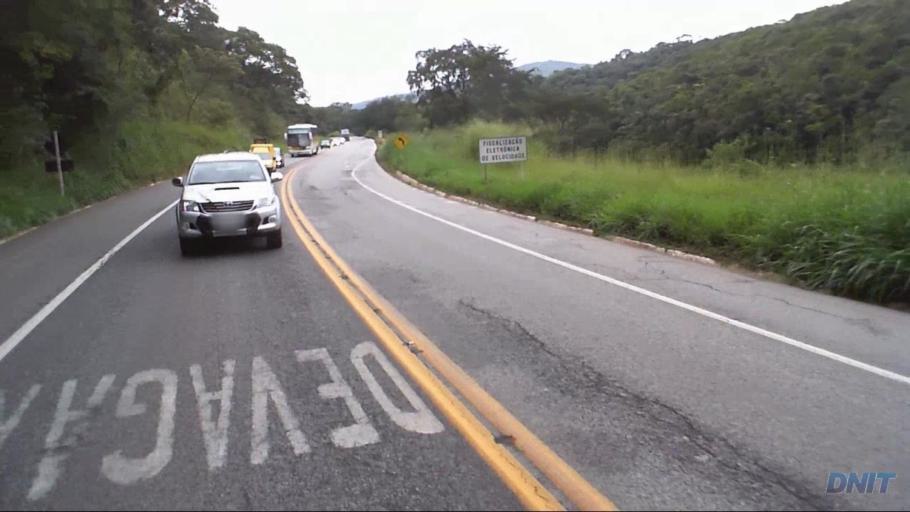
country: BR
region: Minas Gerais
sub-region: Joao Monlevade
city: Joao Monlevade
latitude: -19.8370
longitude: -43.3441
